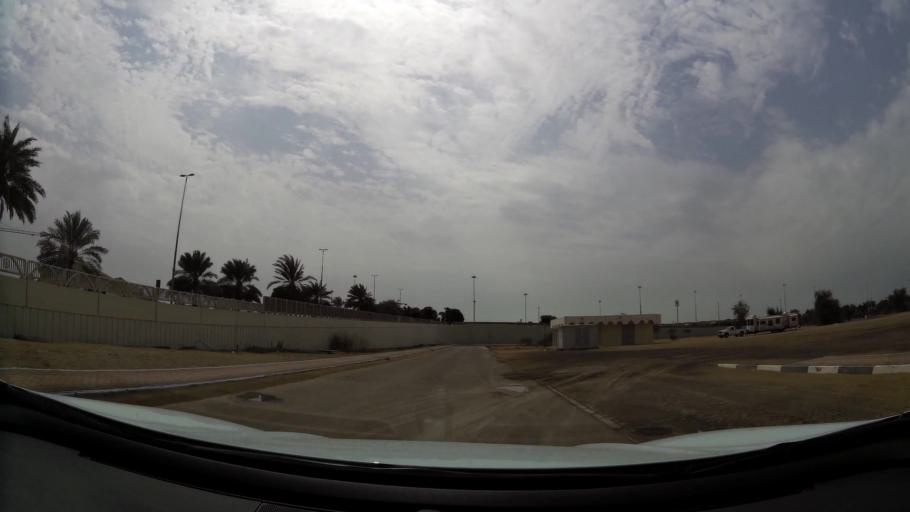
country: AE
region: Abu Dhabi
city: Abu Dhabi
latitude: 24.4101
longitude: 54.4718
